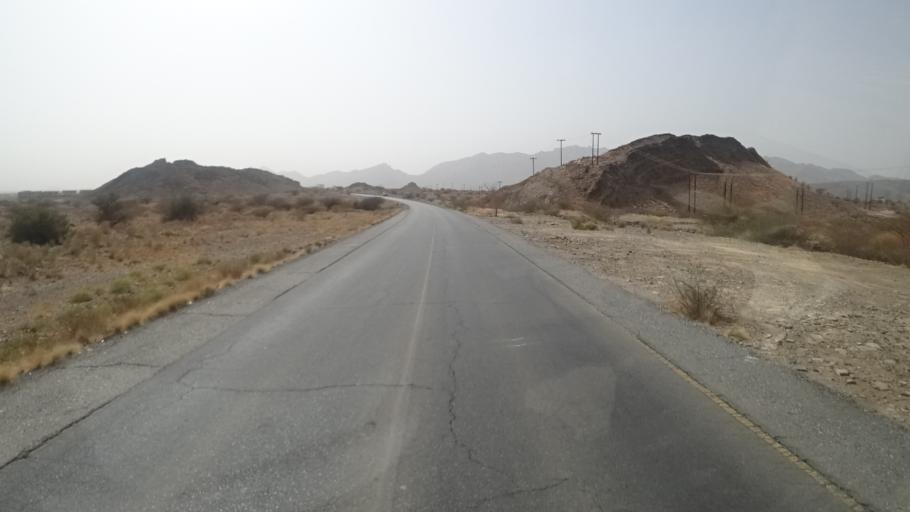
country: OM
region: Muhafazat ad Dakhiliyah
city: Nizwa
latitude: 22.9261
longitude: 57.6283
